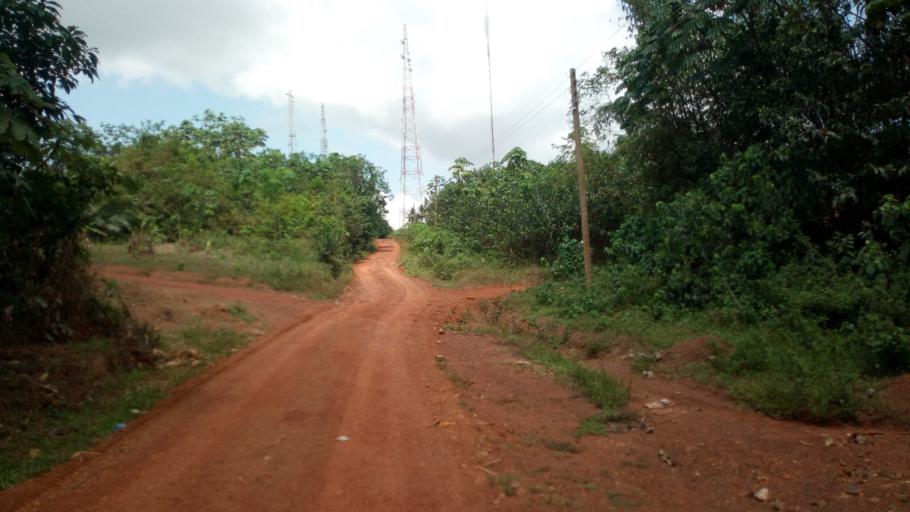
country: GH
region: Western
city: Tarkwa
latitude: 5.3012
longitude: -2.0048
